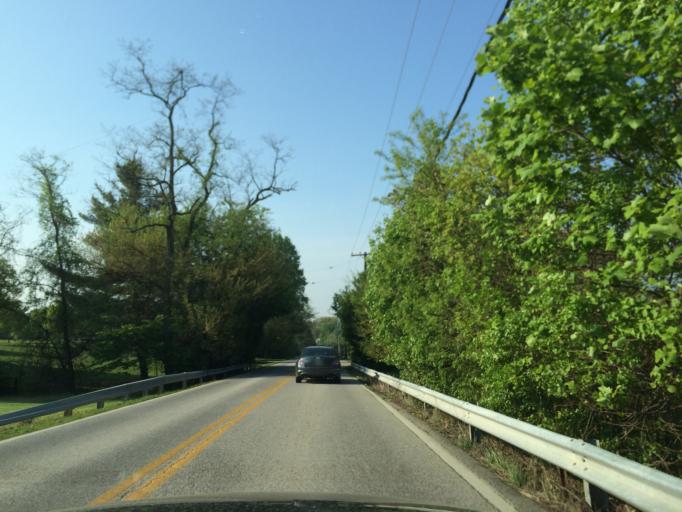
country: US
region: Maryland
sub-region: Howard County
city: Highland
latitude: 39.2517
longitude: -76.9836
